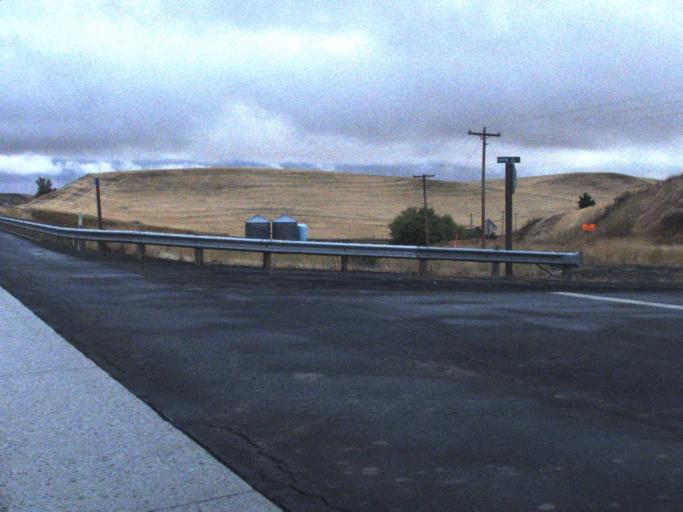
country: US
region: Washington
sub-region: Whitman County
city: Colfax
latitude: 47.0305
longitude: -117.3626
